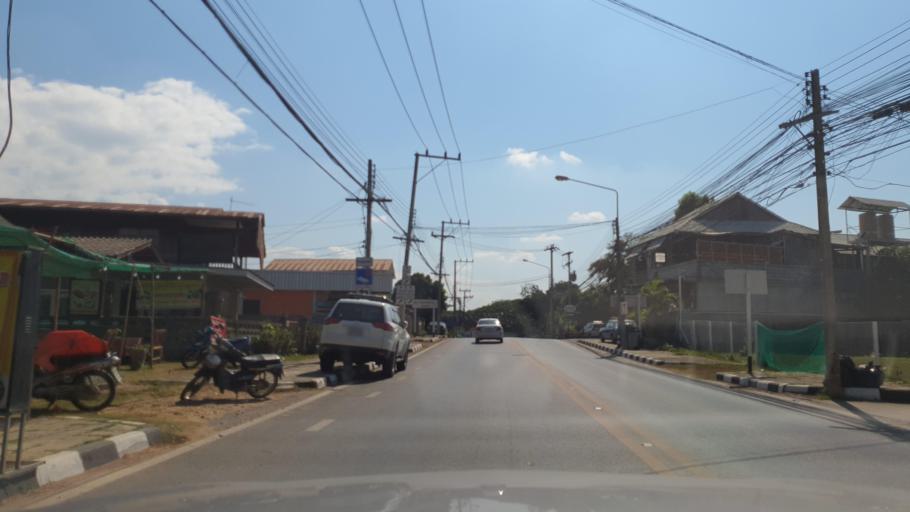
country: TH
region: Nan
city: Nan
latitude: 18.7934
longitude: 100.7798
